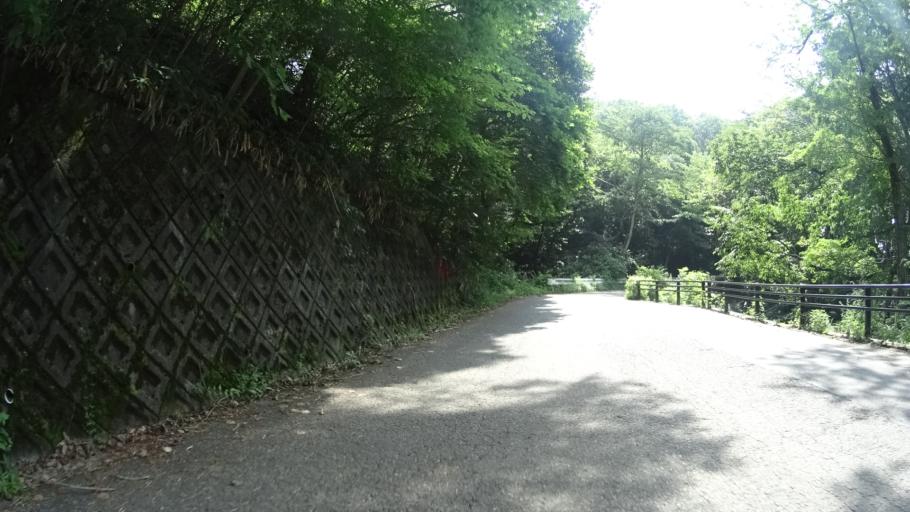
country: JP
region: Yamanashi
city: Nirasaki
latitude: 35.9113
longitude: 138.4224
